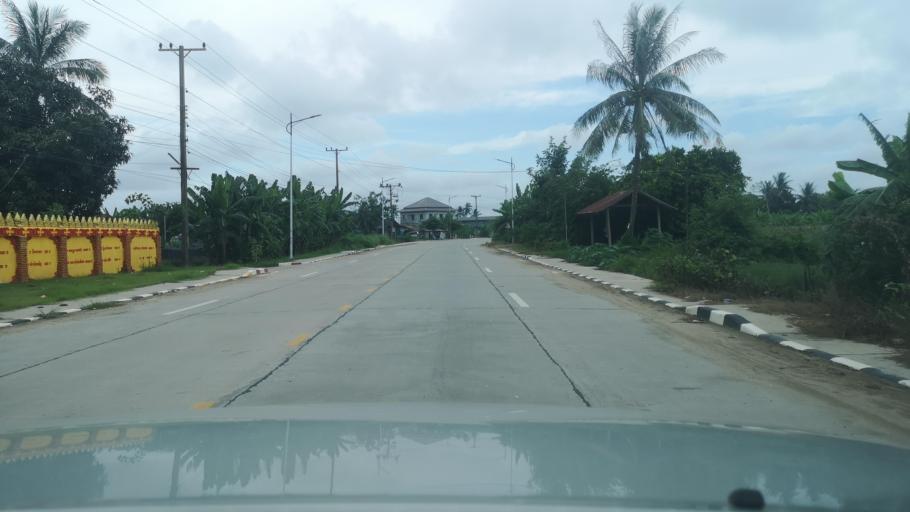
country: TH
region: Nong Khai
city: Tha Bo
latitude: 17.8222
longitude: 102.6627
